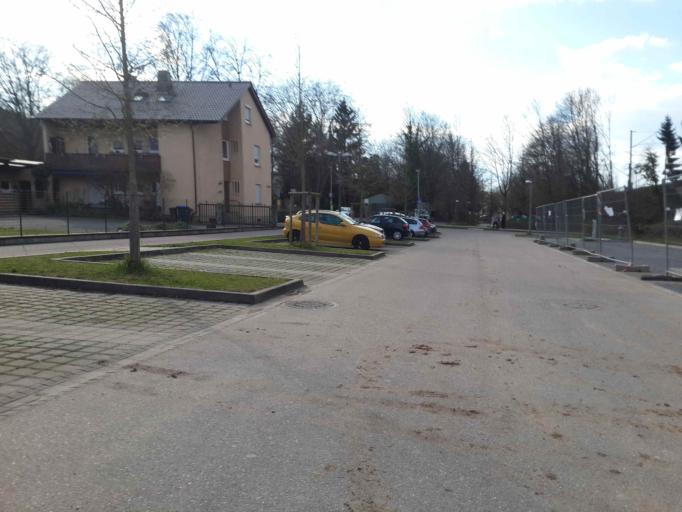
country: DE
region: Baden-Wuerttemberg
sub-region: Regierungsbezirk Stuttgart
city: Weinsberg
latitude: 49.1487
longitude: 9.2840
